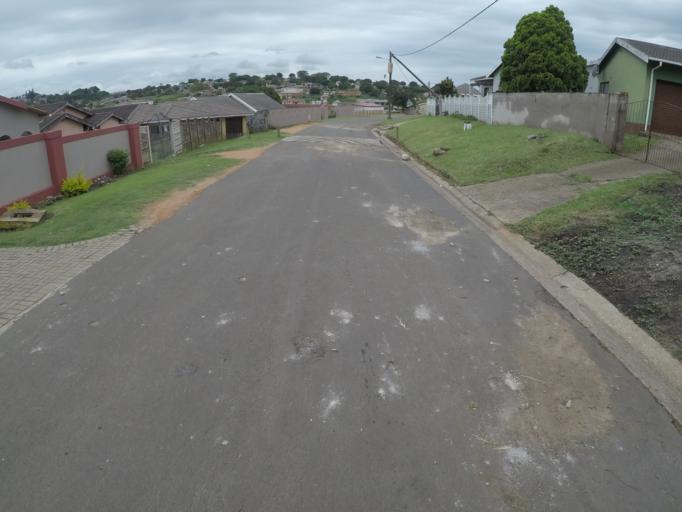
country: ZA
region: KwaZulu-Natal
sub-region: uThungulu District Municipality
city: Empangeni
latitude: -28.7774
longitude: 31.8560
